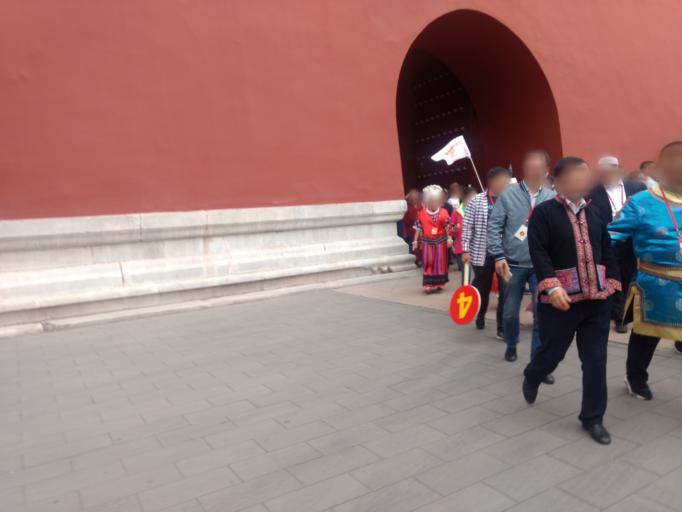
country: CN
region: Beijing
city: Beijing
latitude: 39.9087
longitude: 116.3911
